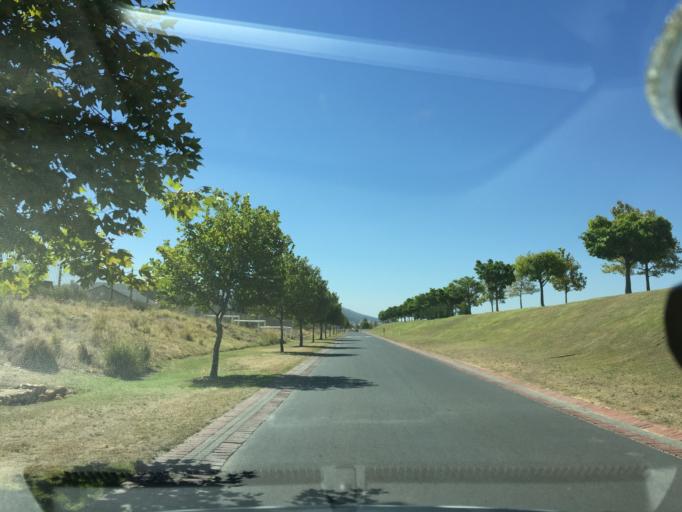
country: ZA
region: Western Cape
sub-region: Cape Winelands District Municipality
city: Paarl
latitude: -33.8085
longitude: 18.9739
